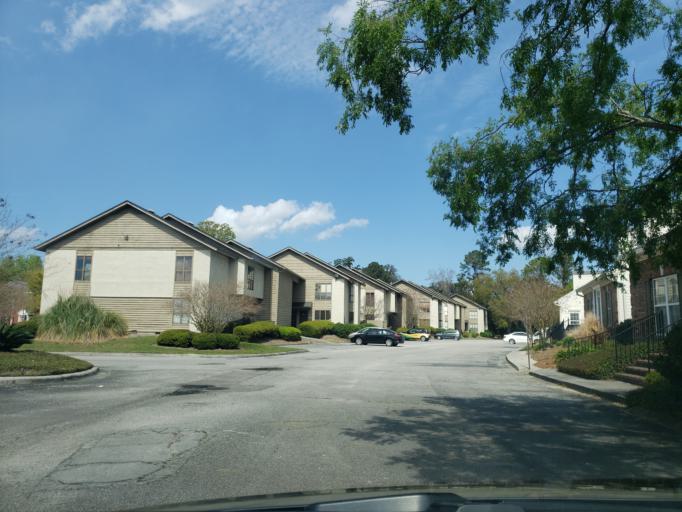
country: US
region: Georgia
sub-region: Chatham County
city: Isle of Hope
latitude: 32.0059
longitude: -81.1073
